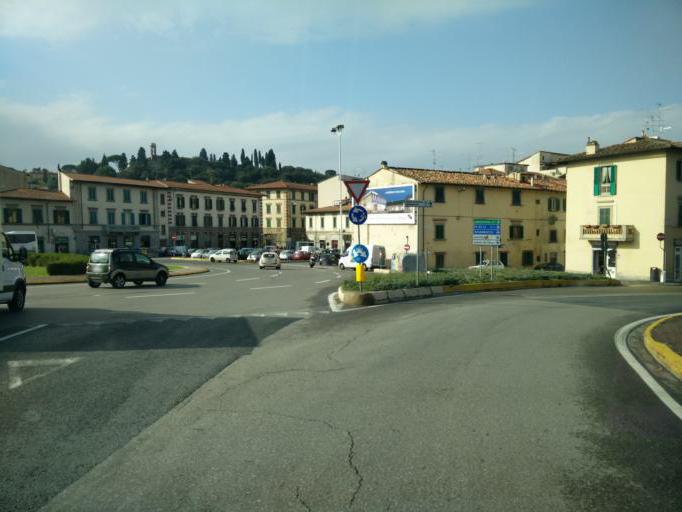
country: IT
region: Tuscany
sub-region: Province of Florence
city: Florence
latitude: 43.7744
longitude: 11.2342
